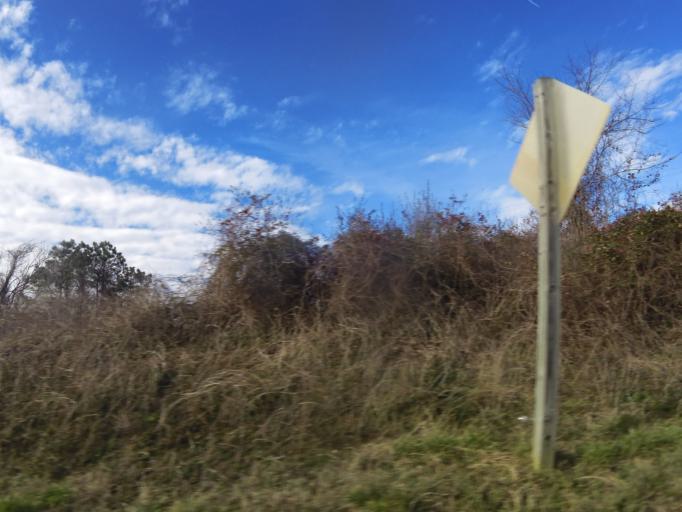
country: US
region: Virginia
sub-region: City of Franklin
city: Franklin
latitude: 36.6844
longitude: -76.9103
